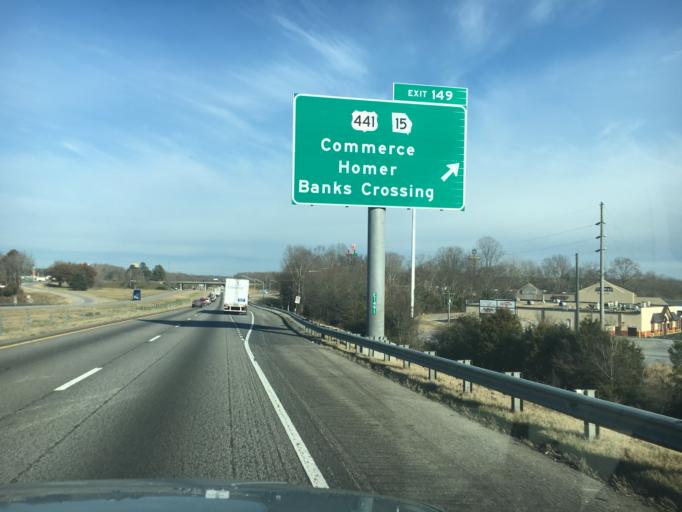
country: US
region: Georgia
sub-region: Jackson County
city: Commerce
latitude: 34.2519
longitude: -83.4681
